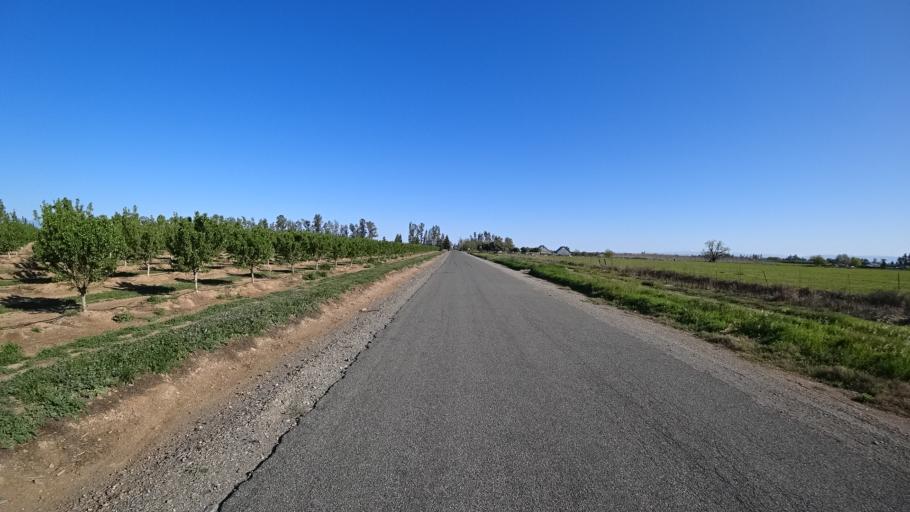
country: US
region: California
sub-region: Glenn County
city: Orland
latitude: 39.7340
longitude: -122.2391
